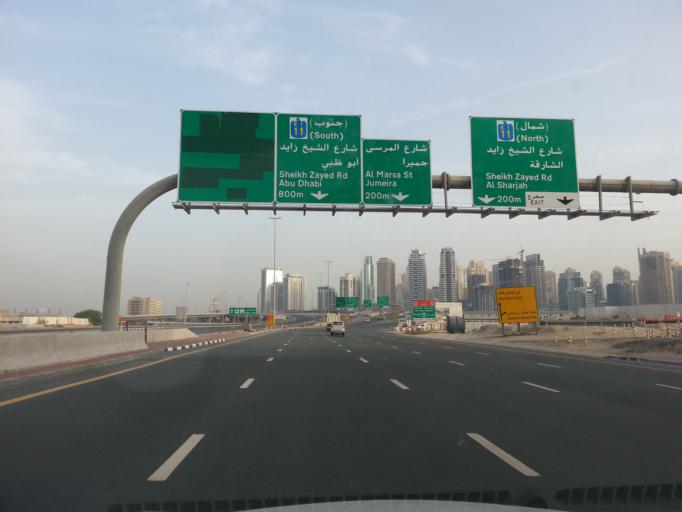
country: AE
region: Dubai
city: Dubai
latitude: 25.0603
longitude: 55.1371
